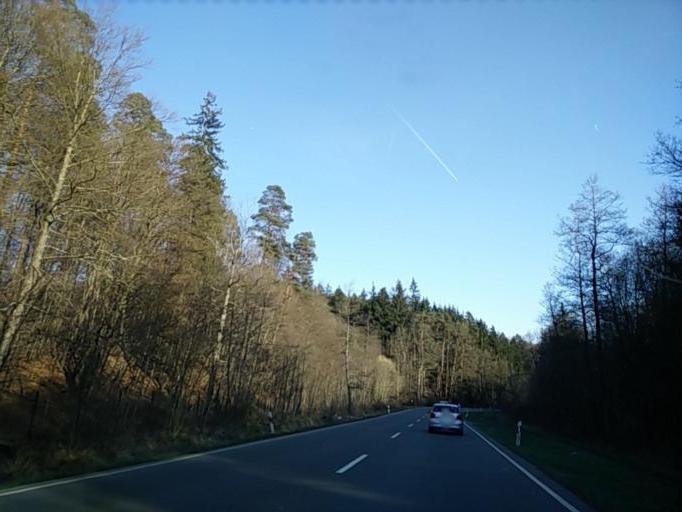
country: DE
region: Baden-Wuerttemberg
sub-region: Tuebingen Region
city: Dettenhausen
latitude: 48.5712
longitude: 9.0725
